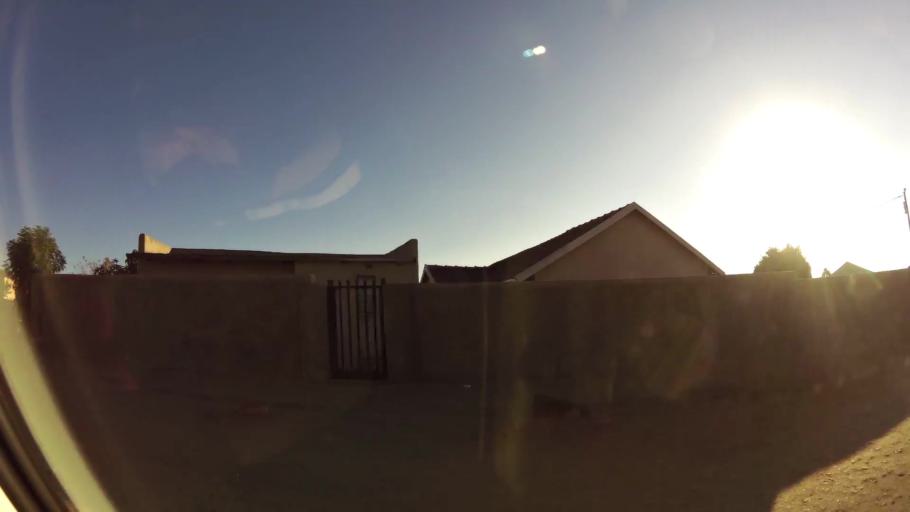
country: ZA
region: Limpopo
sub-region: Capricorn District Municipality
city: Polokwane
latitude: -23.8449
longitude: 29.3579
